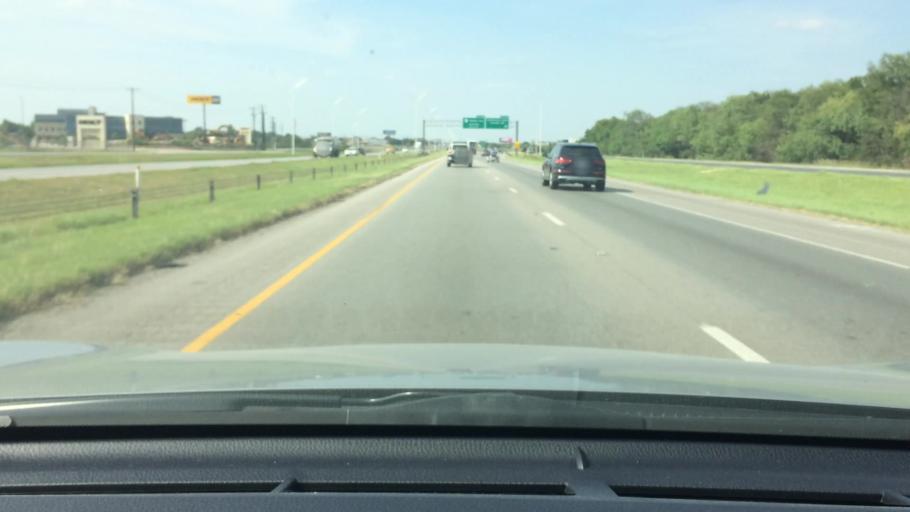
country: US
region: Texas
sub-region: Bexar County
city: China Grove
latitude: 29.3673
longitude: -98.3963
